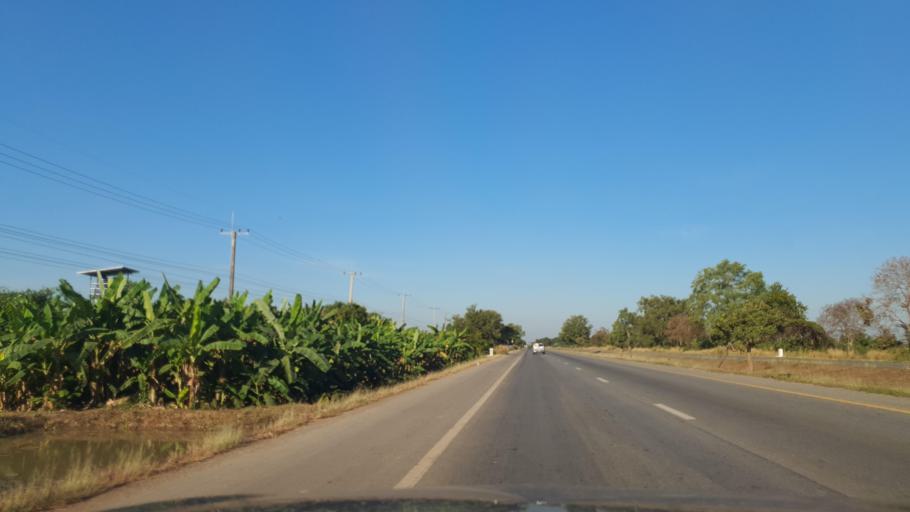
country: TH
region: Sukhothai
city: Sukhothai
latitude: 17.0693
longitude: 99.8561
